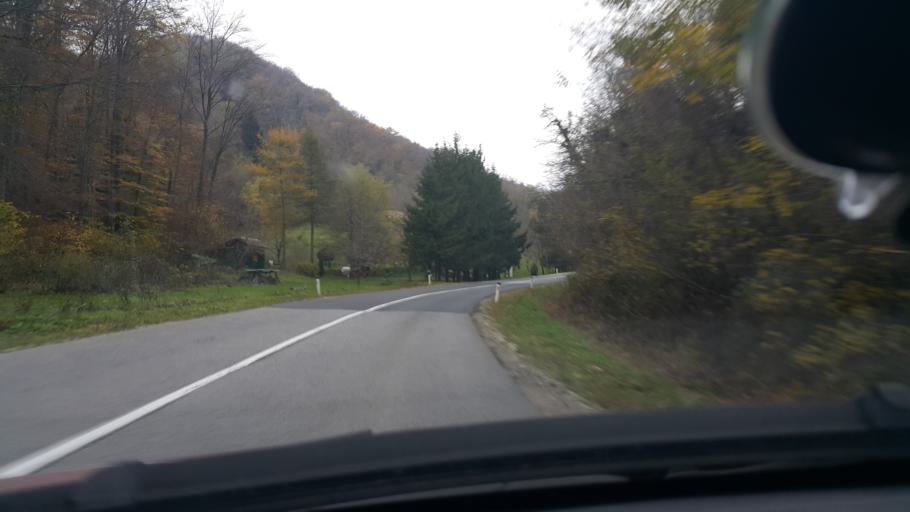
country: SI
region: Bistrica ob Sotli
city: Bistrica ob Sotli
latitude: 46.0442
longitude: 15.6842
